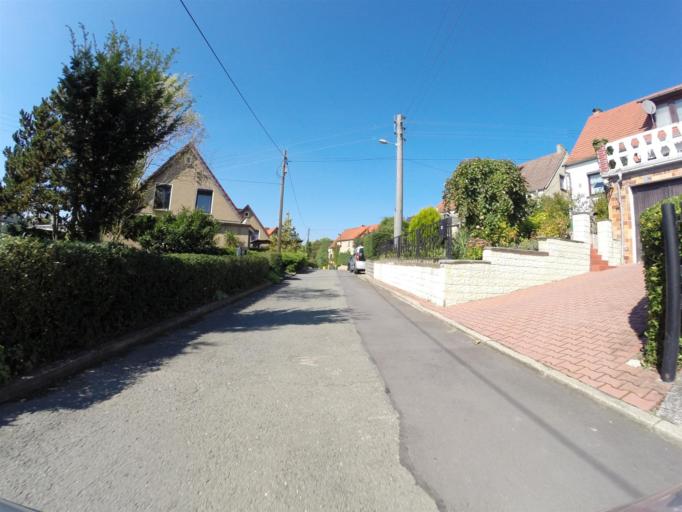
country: DE
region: Thuringia
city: Sulza
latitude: 50.8940
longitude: 11.6127
